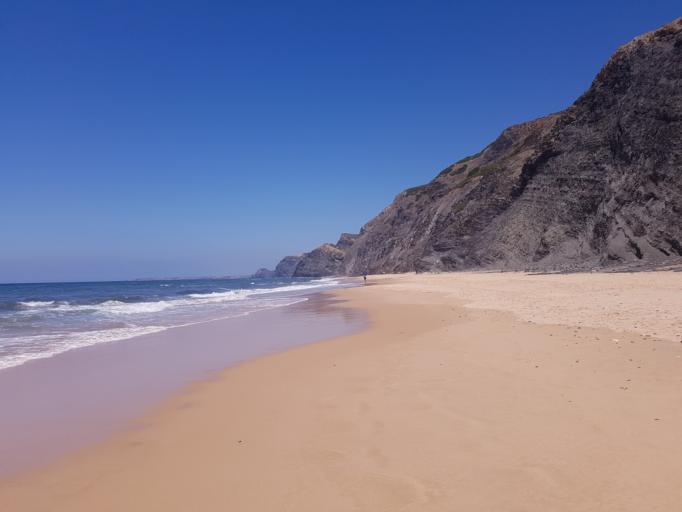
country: PT
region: Faro
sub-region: Vila do Bispo
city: Vila do Bispo
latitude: 37.1126
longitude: -8.9350
